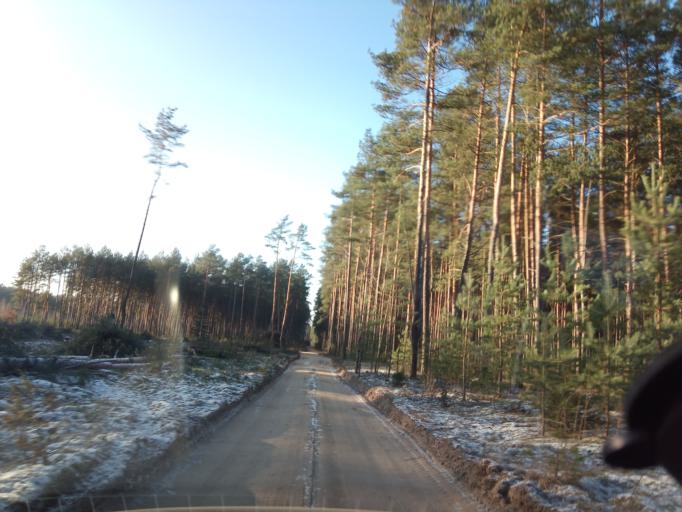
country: LT
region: Alytaus apskritis
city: Druskininkai
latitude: 53.9566
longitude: 23.8773
